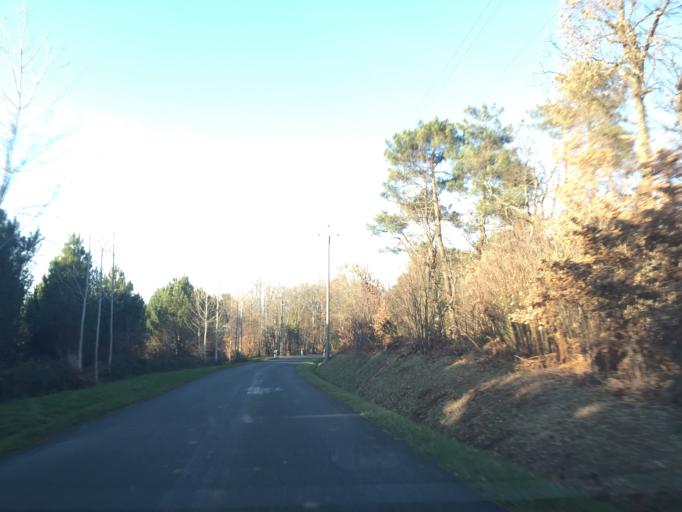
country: FR
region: Aquitaine
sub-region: Departement de la Dordogne
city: Riberac
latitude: 45.2146
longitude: 0.2952
